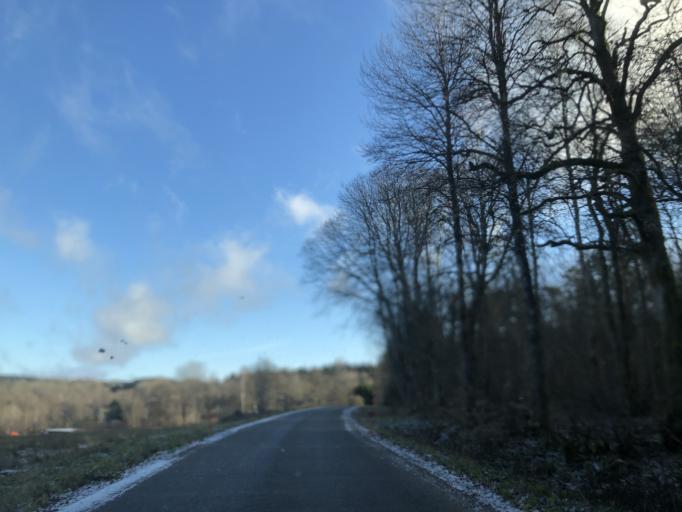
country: SE
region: Vaestra Goetaland
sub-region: Ulricehamns Kommun
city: Ulricehamn
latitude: 57.7285
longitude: 13.4287
